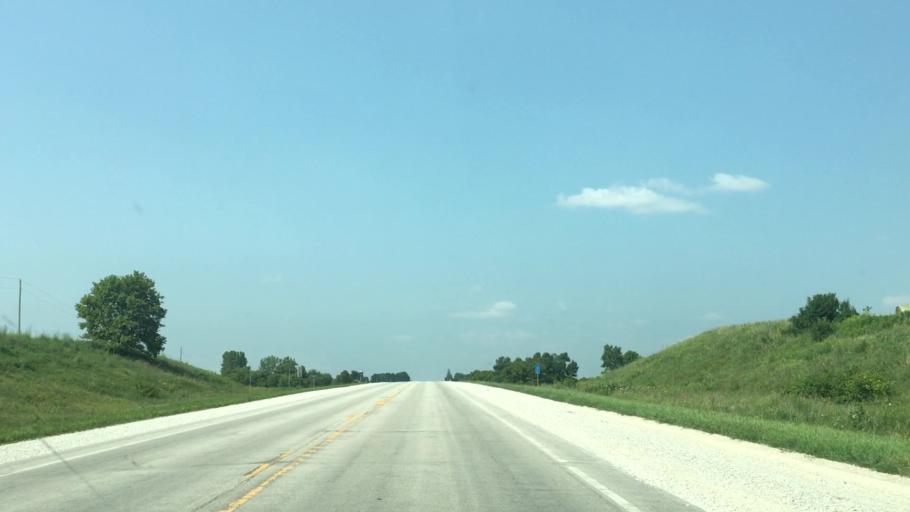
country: US
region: Minnesota
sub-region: Fillmore County
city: Harmony
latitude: 43.4603
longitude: -91.8697
